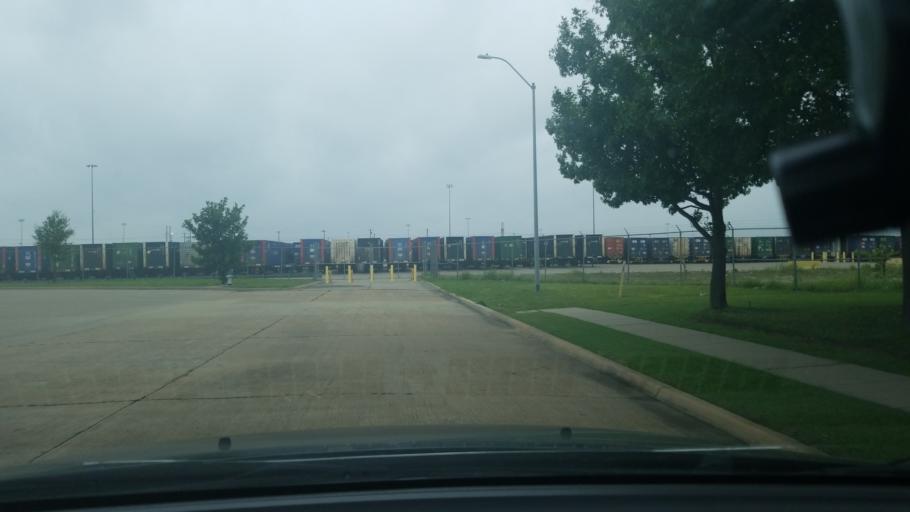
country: US
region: Texas
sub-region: Dallas County
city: Mesquite
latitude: 32.7868
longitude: -96.6591
